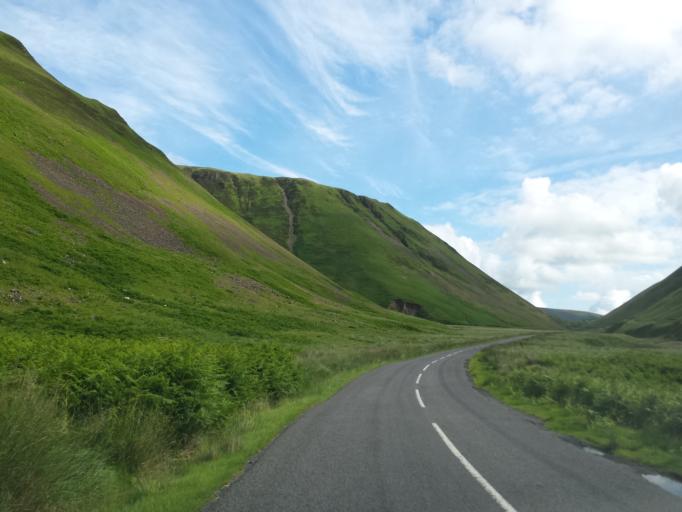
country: GB
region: Scotland
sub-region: Dumfries and Galloway
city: Moffat
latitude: 55.4140
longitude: -3.2932
